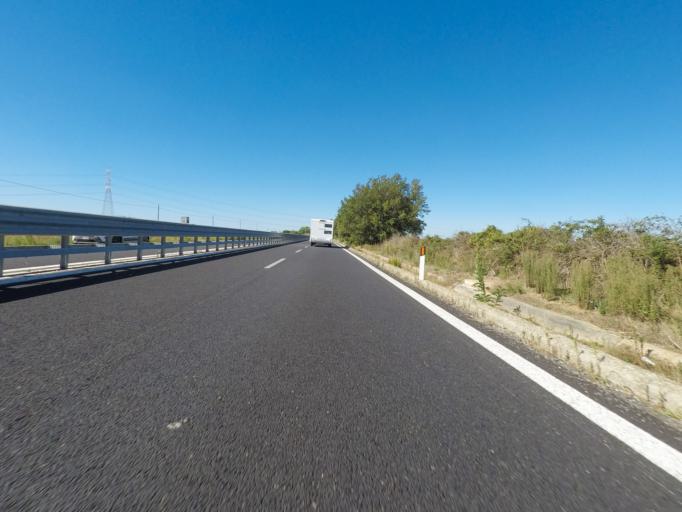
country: IT
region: Latium
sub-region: Provincia di Viterbo
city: Tarquinia
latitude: 42.2762
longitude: 11.7043
